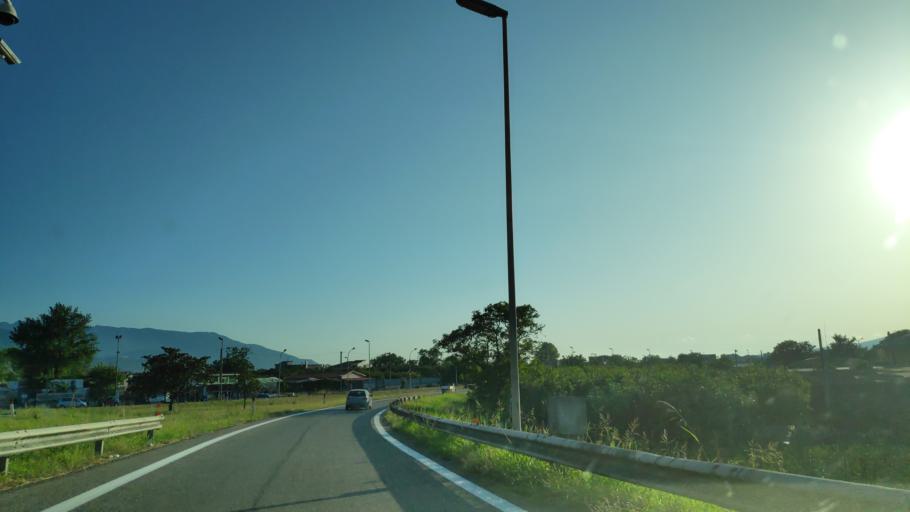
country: IT
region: Campania
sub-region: Provincia di Salerno
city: San Valentino Torio
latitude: 40.7752
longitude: 14.6143
